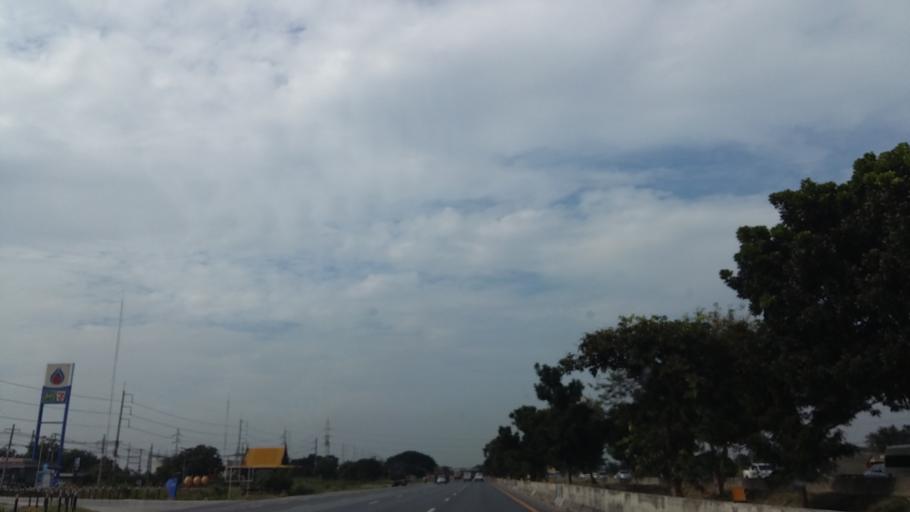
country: TH
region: Phra Nakhon Si Ayutthaya
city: Maha Rat
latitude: 14.5013
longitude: 100.5213
